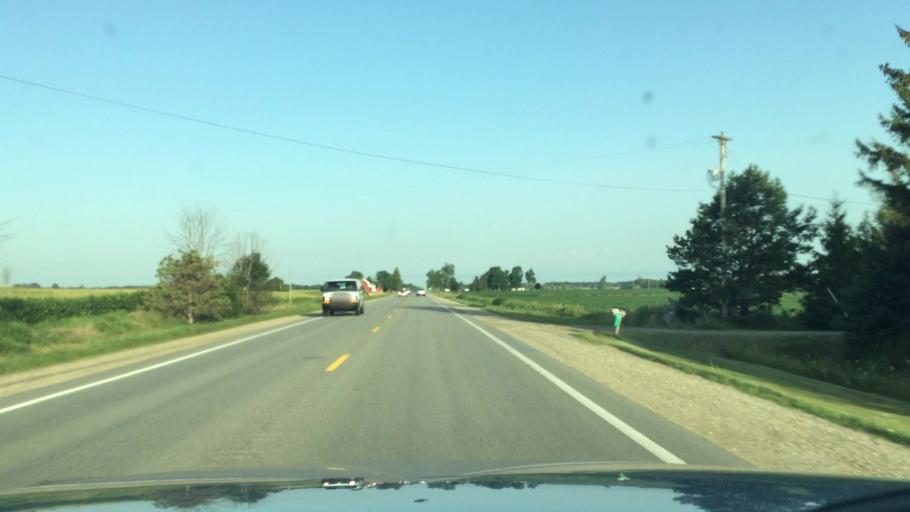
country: US
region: Michigan
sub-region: Gratiot County
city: Ithaca
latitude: 43.1760
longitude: -84.5894
